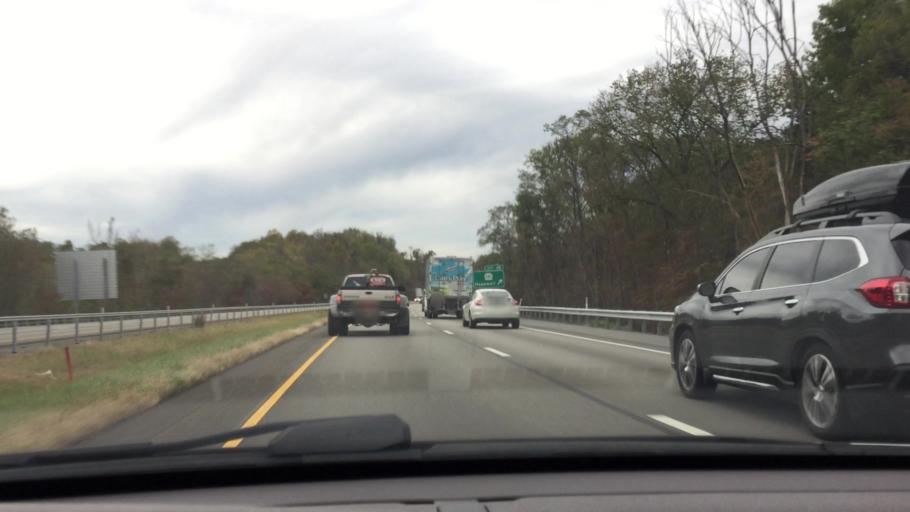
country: US
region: Pennsylvania
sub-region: Beaver County
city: Ambridge
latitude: 40.5517
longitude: -80.2772
